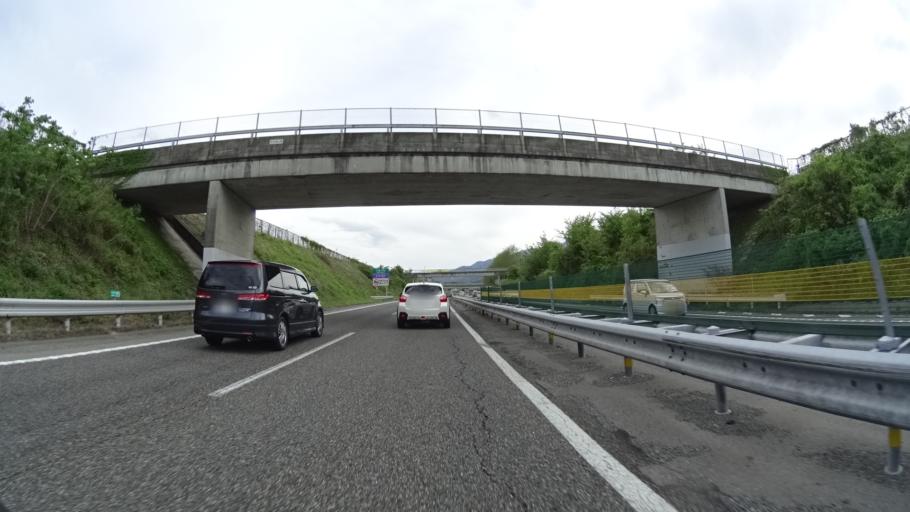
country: JP
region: Nagano
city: Ina
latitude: 35.8461
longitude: 137.9356
